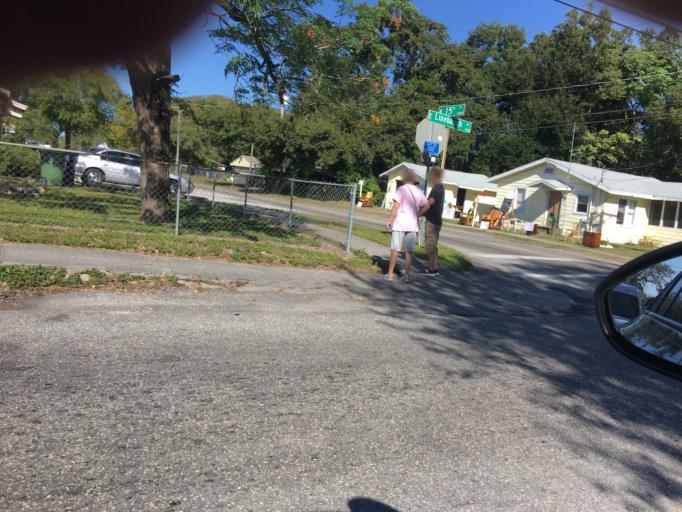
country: US
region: Florida
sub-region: Hillsborough County
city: University
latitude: 28.0399
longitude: -82.4431
